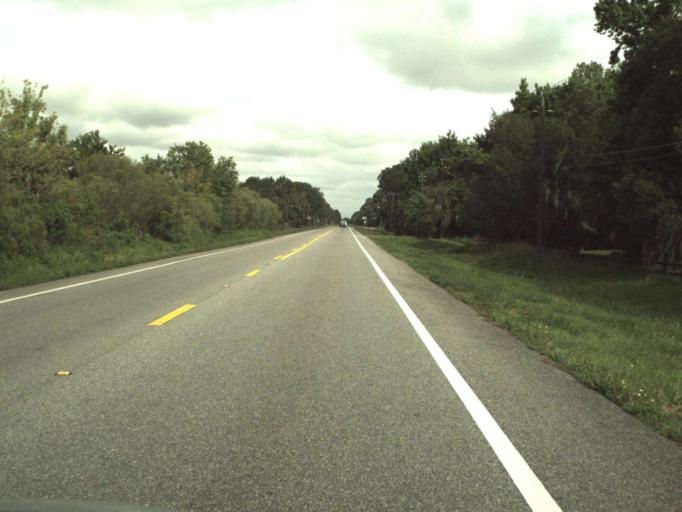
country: US
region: Florida
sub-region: Seminole County
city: Geneva
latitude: 28.7639
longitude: -81.1492
